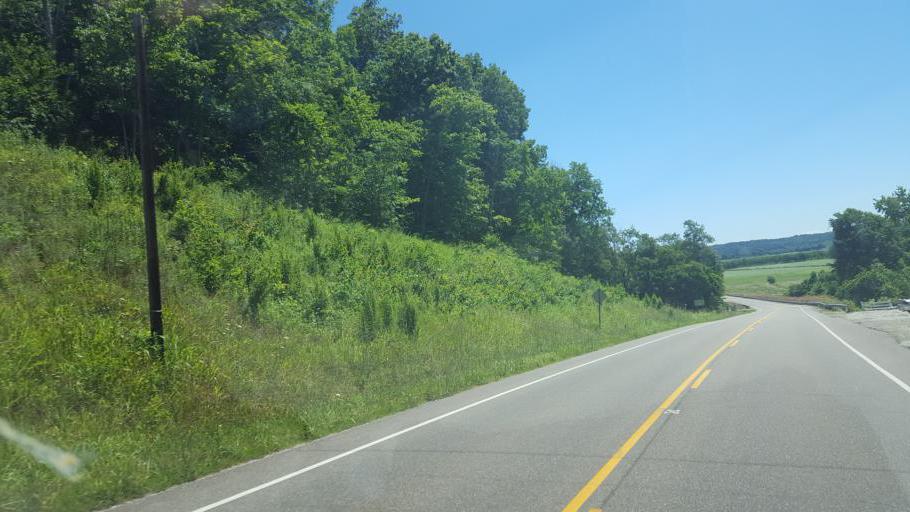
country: US
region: West Virginia
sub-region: Cabell County
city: Lesage
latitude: 38.6000
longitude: -82.2447
